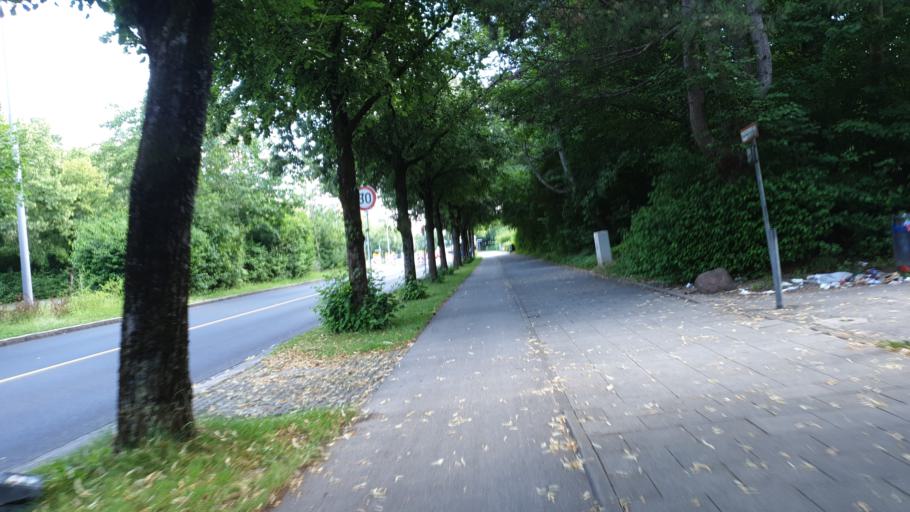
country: DE
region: Bavaria
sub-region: Upper Bavaria
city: Neubiberg
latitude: 48.1045
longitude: 11.6364
